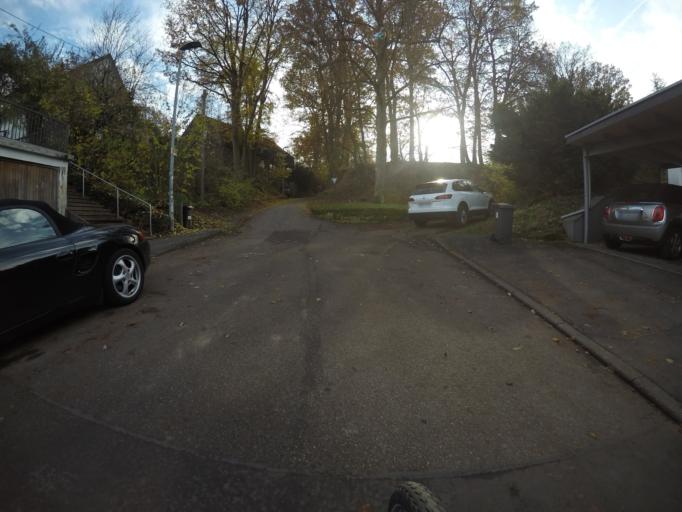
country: DE
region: Baden-Wuerttemberg
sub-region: Regierungsbezirk Stuttgart
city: Steinenbronn
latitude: 48.7031
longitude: 9.1223
